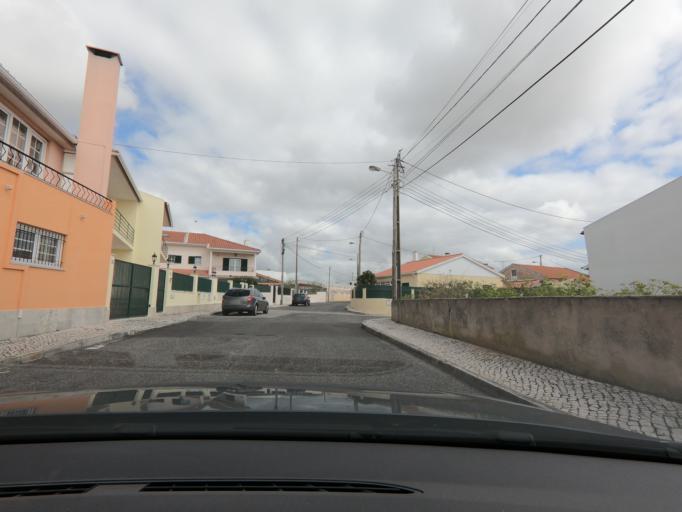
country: PT
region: Lisbon
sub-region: Cascais
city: Sao Domingos de Rana
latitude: 38.7173
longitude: -9.3459
